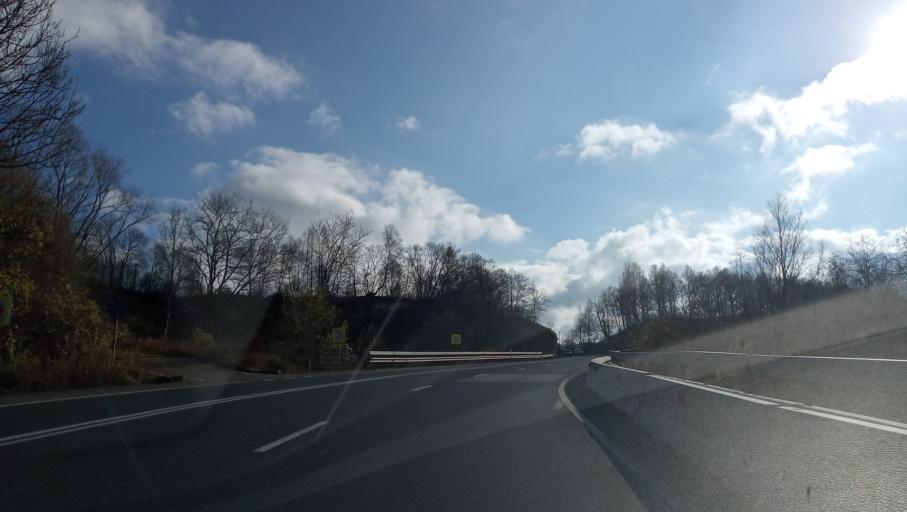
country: RO
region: Hunedoara
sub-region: Comuna Banita
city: Banita
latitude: 45.4581
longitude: 23.2559
